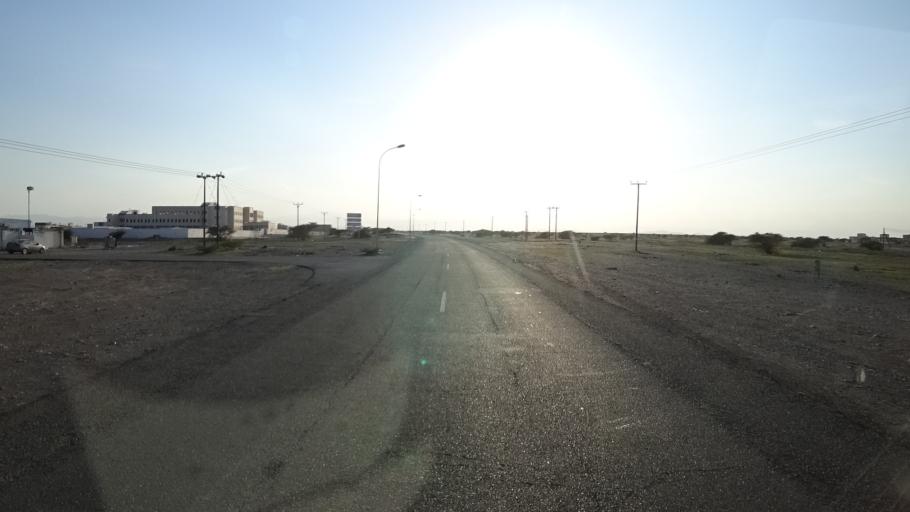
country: OM
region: Al Batinah
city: Al Khaburah
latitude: 23.9467
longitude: 57.0510
